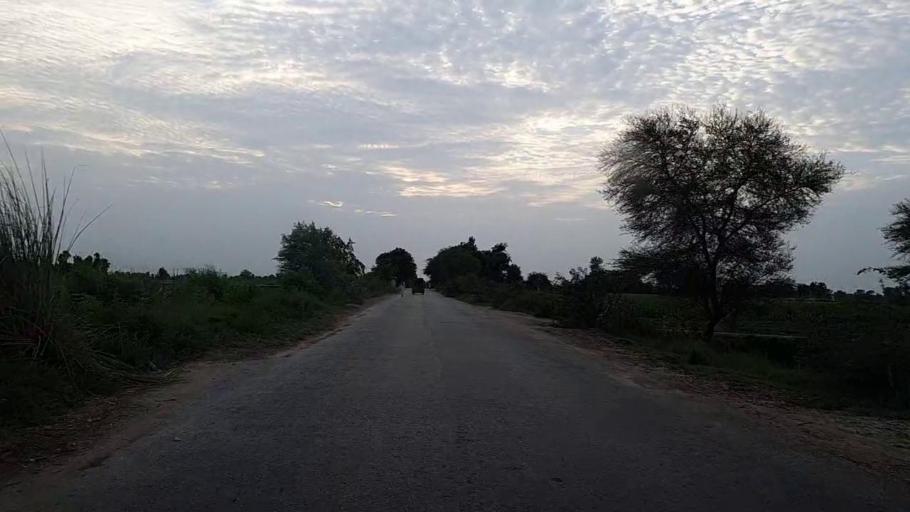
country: PK
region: Sindh
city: Pad Idan
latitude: 26.8055
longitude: 68.2117
